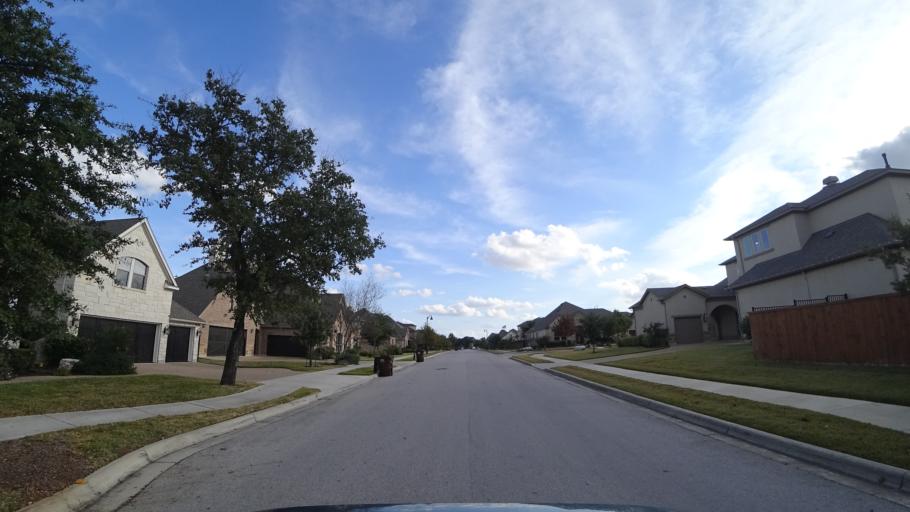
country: US
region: Texas
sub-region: Williamson County
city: Brushy Creek
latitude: 30.5086
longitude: -97.7209
